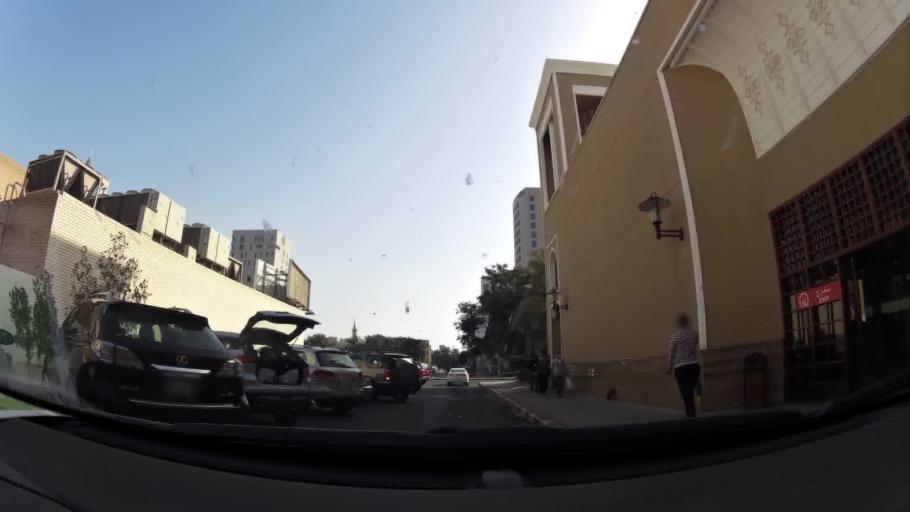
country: KW
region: Muhafazat Hawalli
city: As Salimiyah
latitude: 29.3425
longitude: 48.0750
